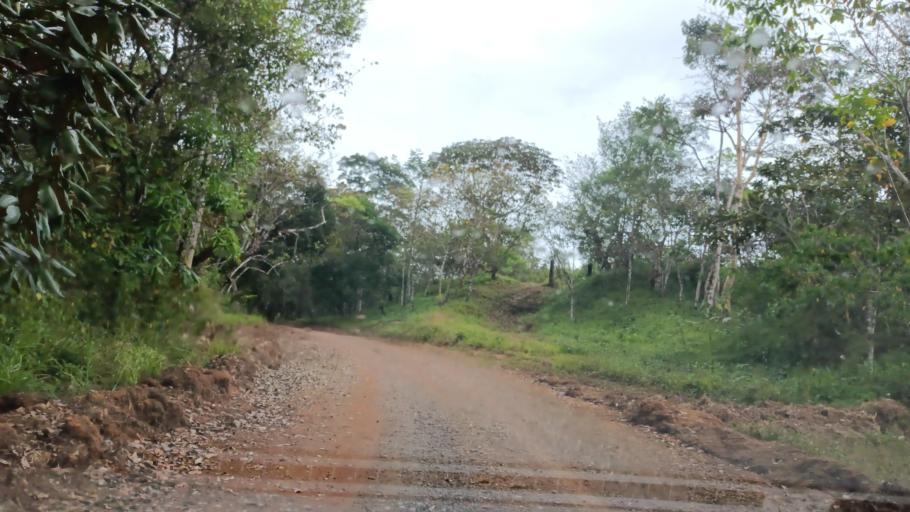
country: PA
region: Panama
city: La Cabima
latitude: 9.1258
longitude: -79.5082
